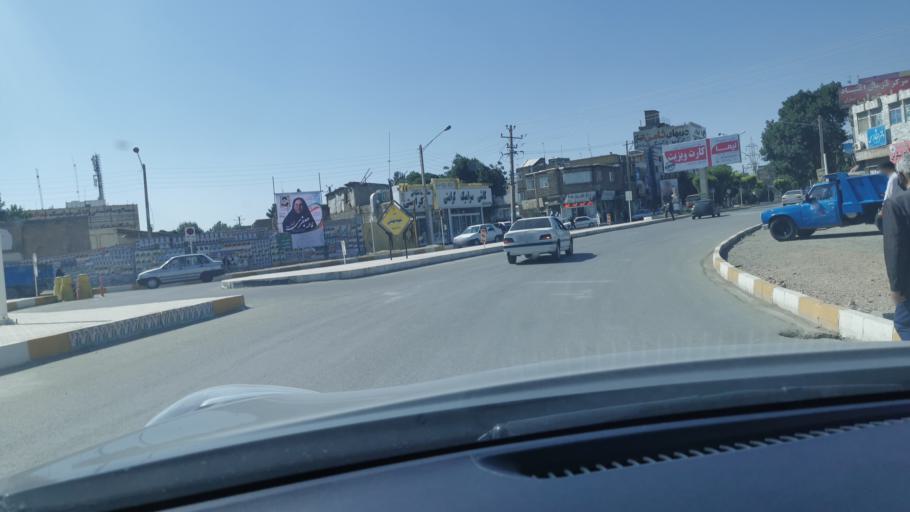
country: IR
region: Razavi Khorasan
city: Chenaran
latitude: 36.6402
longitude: 59.1183
